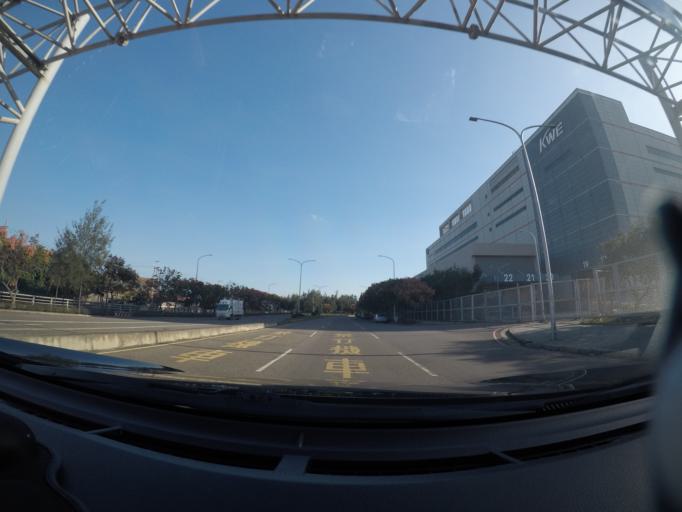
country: TW
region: Taiwan
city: Taoyuan City
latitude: 25.0956
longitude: 121.2571
